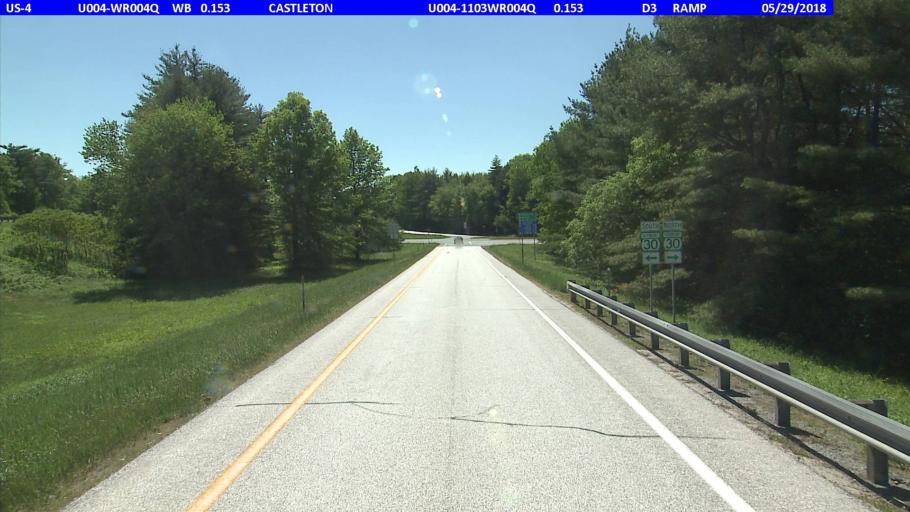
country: US
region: Vermont
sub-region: Rutland County
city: Castleton
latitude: 43.6186
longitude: -73.2045
